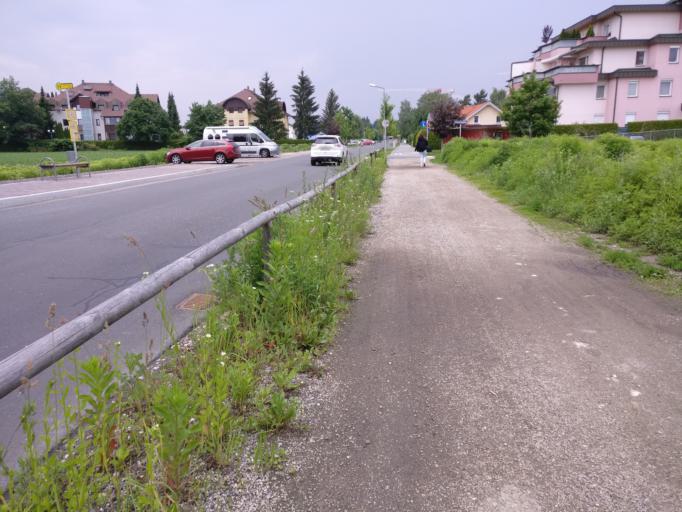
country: AT
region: Carinthia
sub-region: Klagenfurt am Woerthersee
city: Klagenfurt am Woerthersee
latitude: 46.6124
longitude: 14.2747
